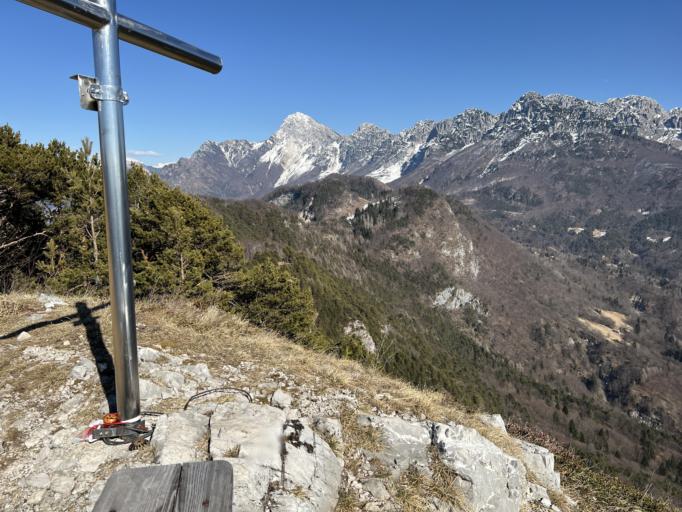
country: IT
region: Friuli Venezia Giulia
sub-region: Provincia di Udine
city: Zuglio
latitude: 46.4401
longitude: 13.0559
